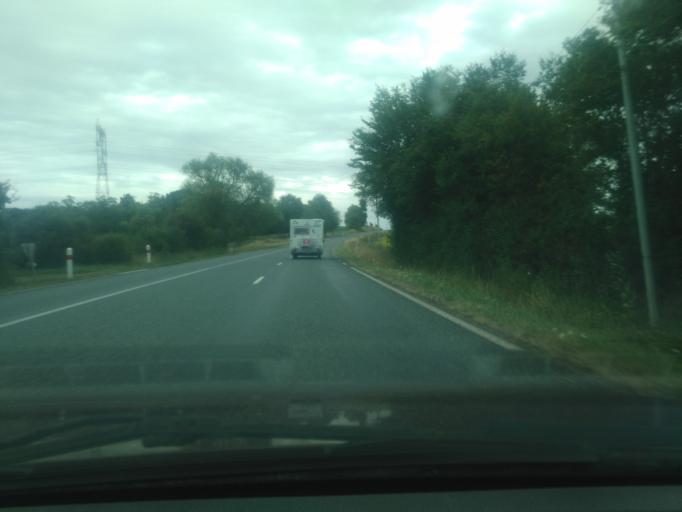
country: FR
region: Auvergne
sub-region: Departement de l'Allier
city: Ainay-le-Chateau
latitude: 46.7570
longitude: 2.7892
